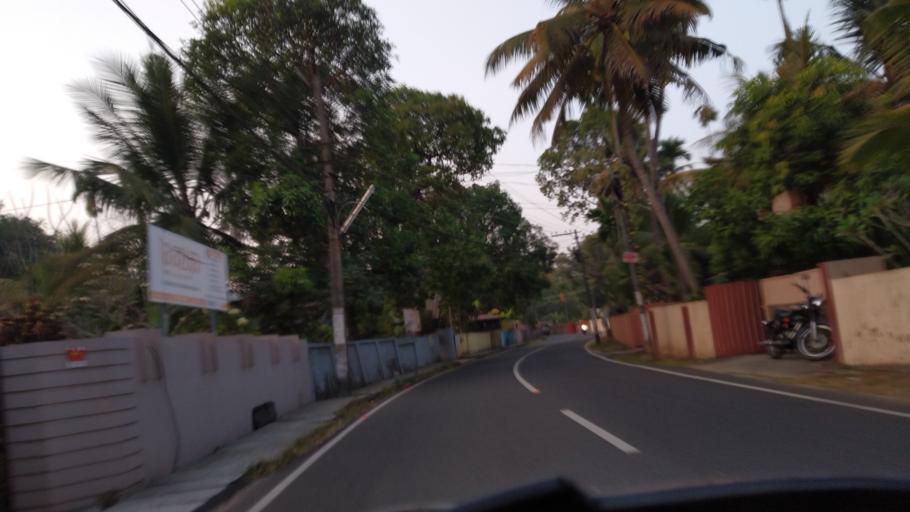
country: IN
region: Kerala
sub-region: Ernakulam
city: Elur
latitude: 10.1325
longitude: 76.2326
